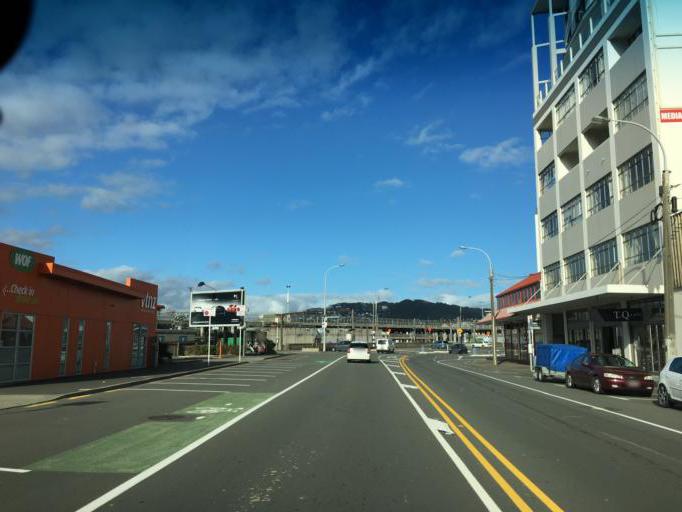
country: NZ
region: Wellington
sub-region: Wellington City
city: Wellington
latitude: -41.2738
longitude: 174.7833
